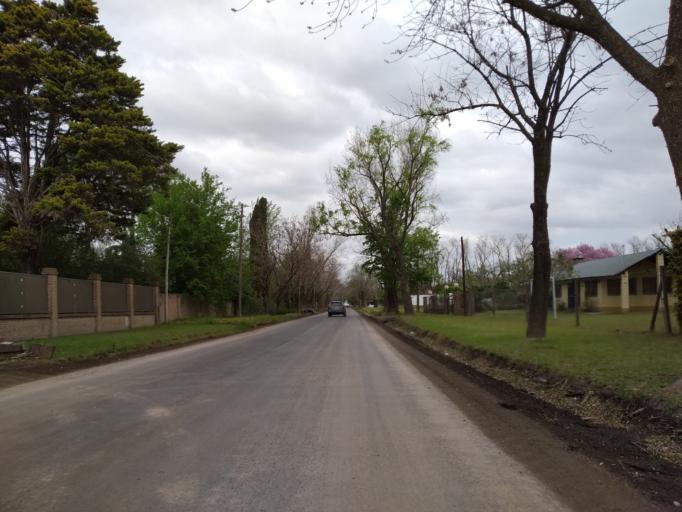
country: AR
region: Santa Fe
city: Funes
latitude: -32.9167
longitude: -60.8514
